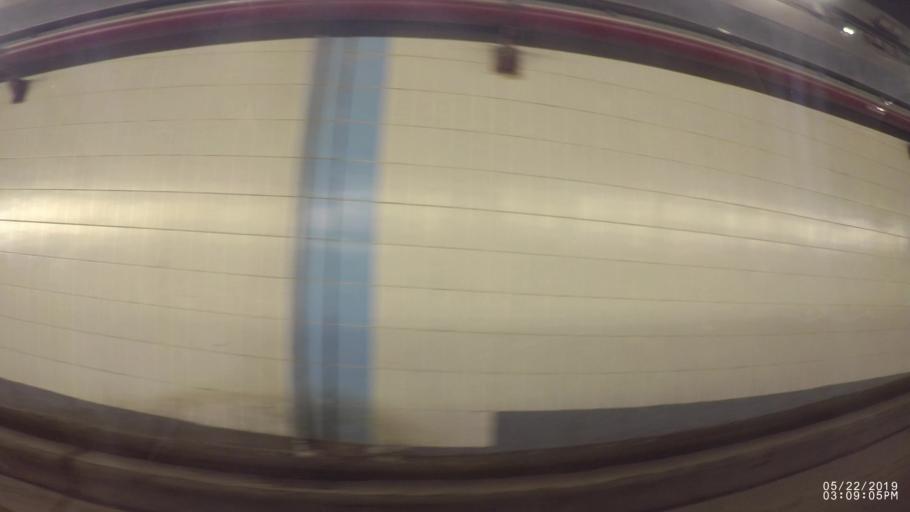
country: LB
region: Beyrouth
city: Beirut
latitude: 33.8831
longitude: 35.4964
